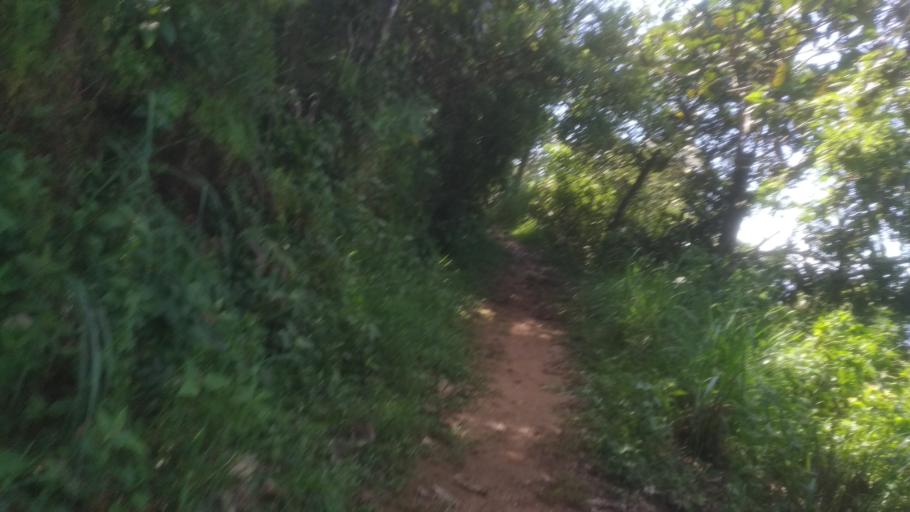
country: IN
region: Kerala
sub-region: Idukki
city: Idukki
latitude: 9.9777
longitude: 76.8352
